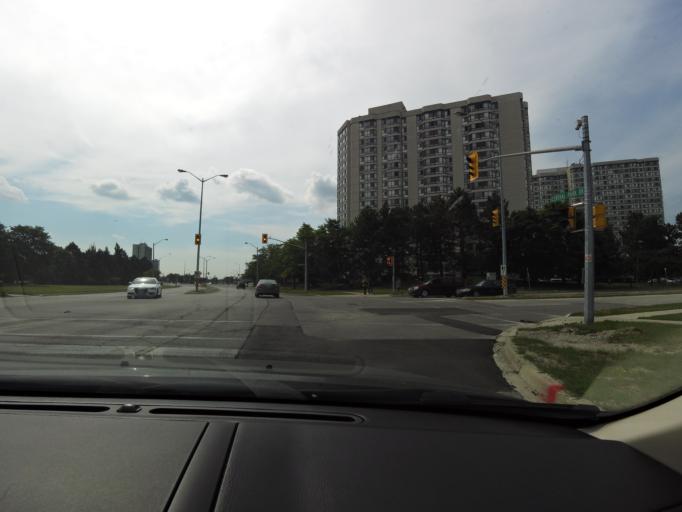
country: CA
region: Ontario
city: Brampton
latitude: 43.7218
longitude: -79.7241
